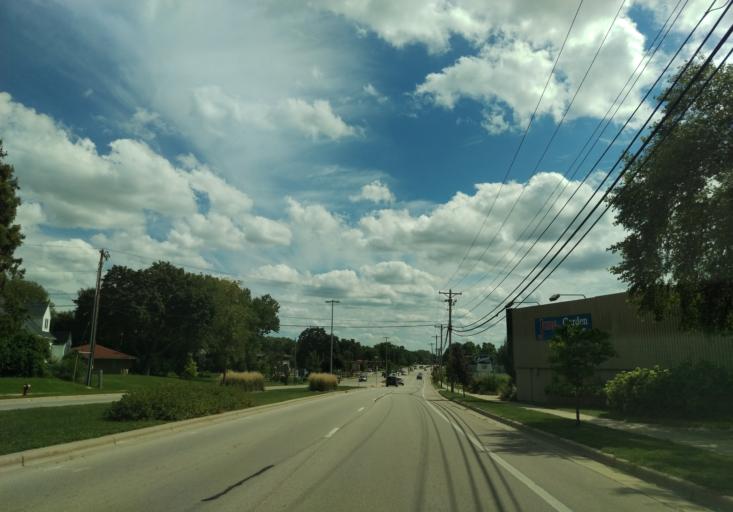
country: US
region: Wisconsin
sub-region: Dane County
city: Maple Bluff
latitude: 43.1352
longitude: -89.3741
